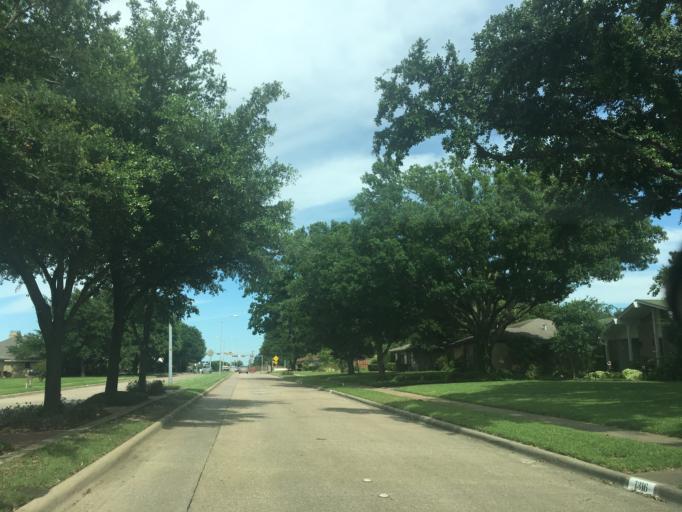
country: US
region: Texas
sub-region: Dallas County
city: Richardson
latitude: 32.9386
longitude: -96.7022
